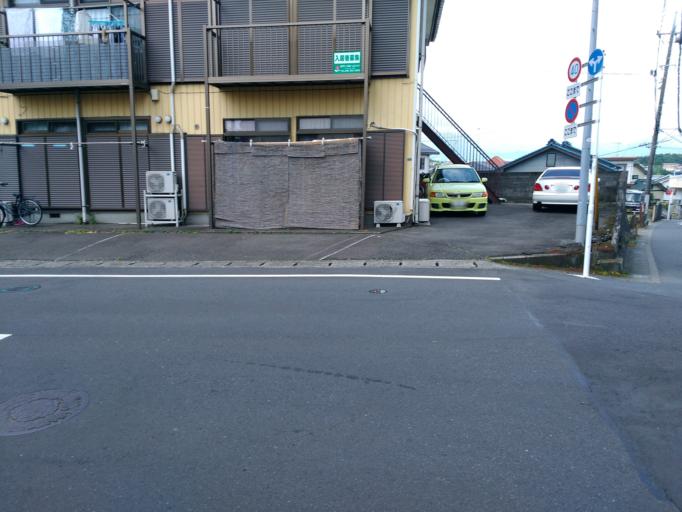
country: JP
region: Kanagawa
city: Atsugi
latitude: 35.4367
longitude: 139.4081
